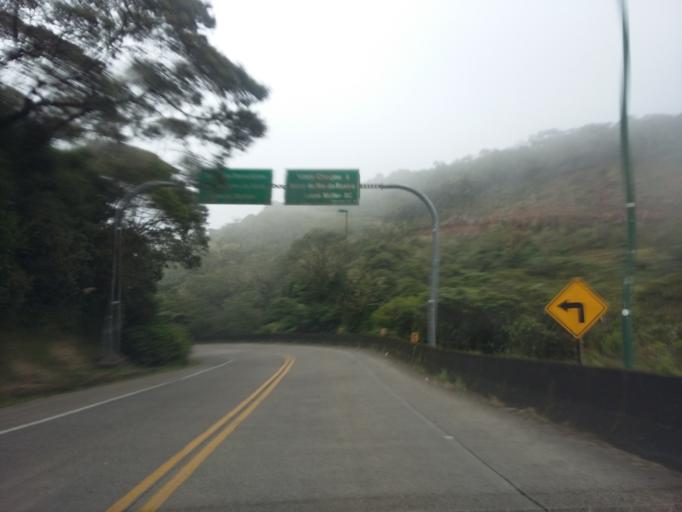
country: BR
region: Santa Catarina
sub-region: Lauro Muller
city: Lauro Muller
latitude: -28.4013
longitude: -49.5501
